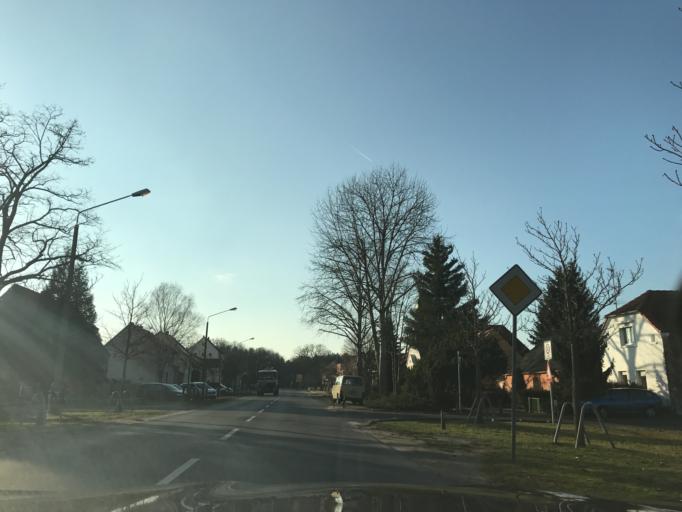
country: DE
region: Brandenburg
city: Brandenburg an der Havel
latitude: 52.3727
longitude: 12.5058
